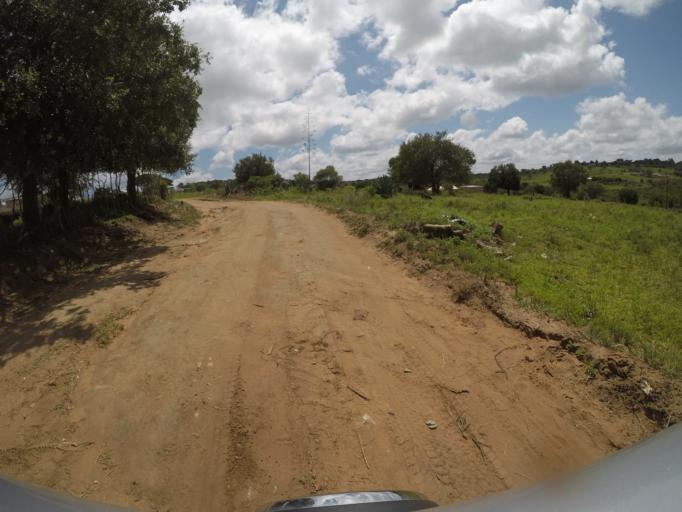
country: ZA
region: KwaZulu-Natal
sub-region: uThungulu District Municipality
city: Empangeni
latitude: -28.5855
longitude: 31.8408
